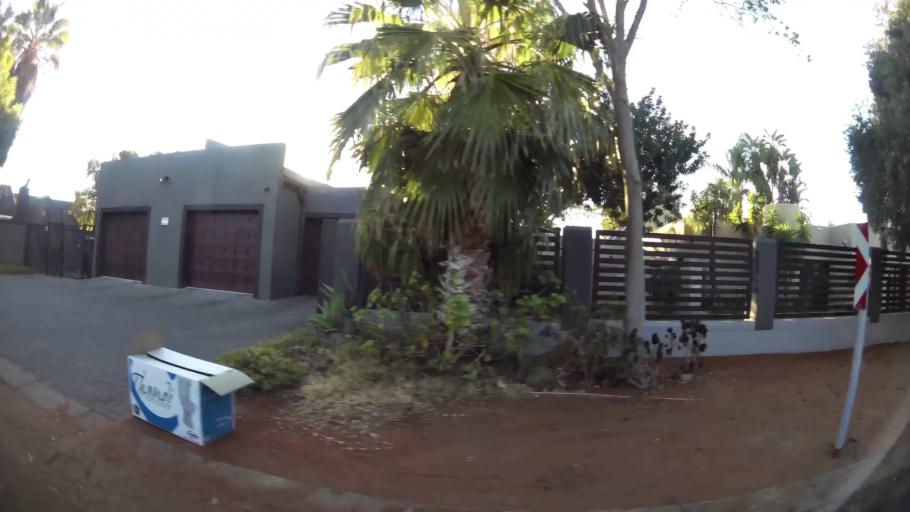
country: ZA
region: Northern Cape
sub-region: Frances Baard District Municipality
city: Kimberley
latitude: -28.7583
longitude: 24.7527
